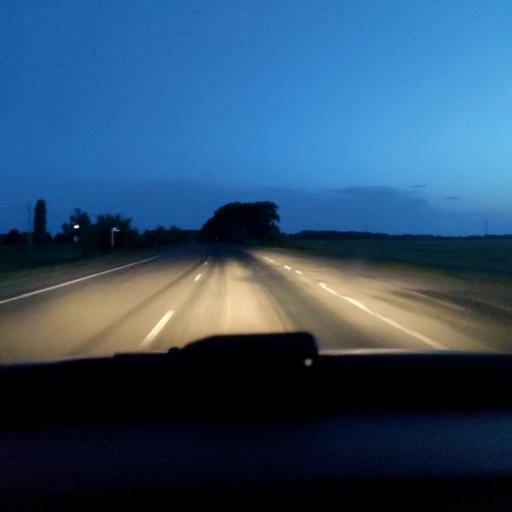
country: RU
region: Voronezj
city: Panino
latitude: 51.6437
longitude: 40.1160
